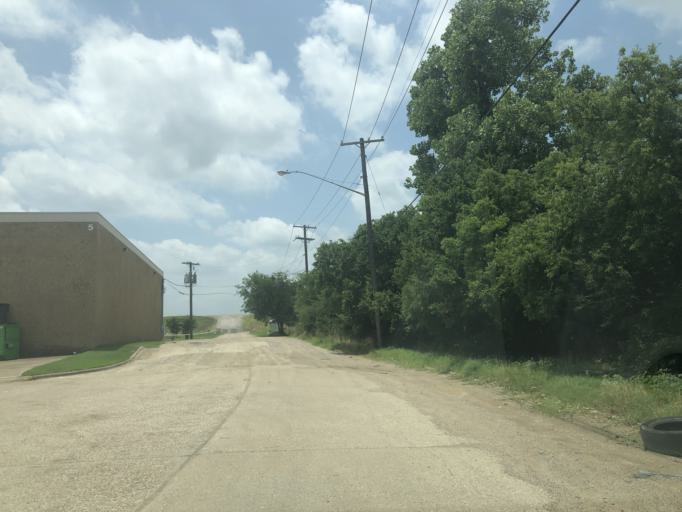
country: US
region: Texas
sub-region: Dallas County
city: Dallas
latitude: 32.8040
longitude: -96.8564
